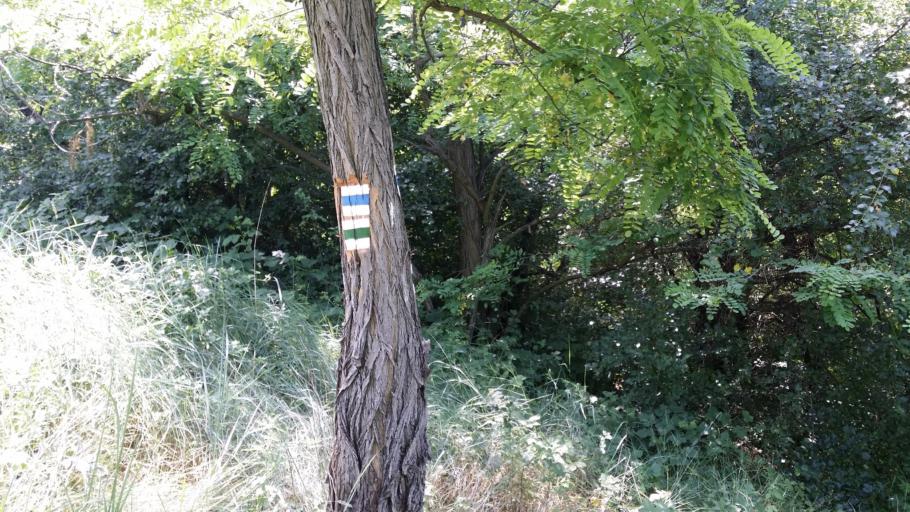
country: HU
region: Komarom-Esztergom
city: Kesztolc
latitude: 47.7234
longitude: 18.7969
